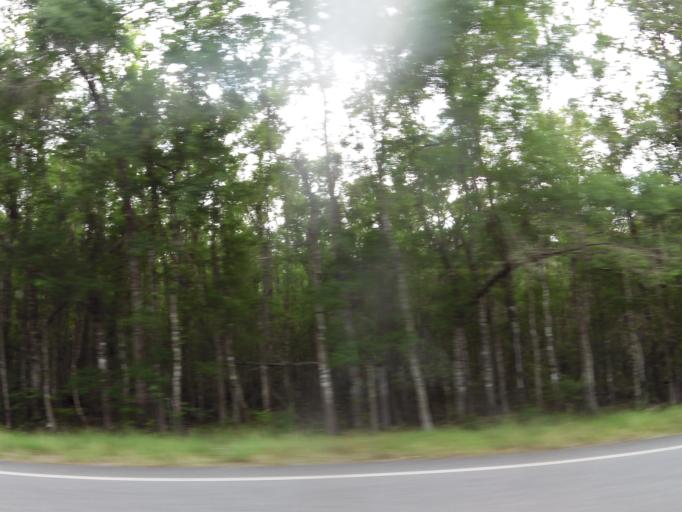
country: US
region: Georgia
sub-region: Charlton County
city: Folkston
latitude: 30.8417
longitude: -81.9063
